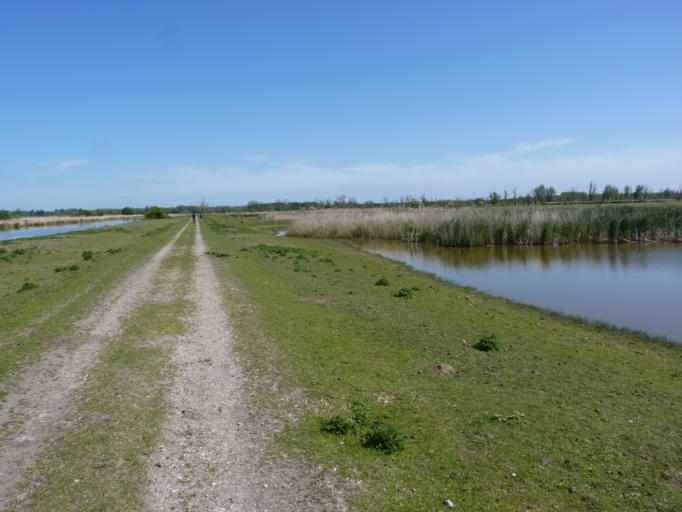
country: NL
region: Flevoland
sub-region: Gemeente Lelystad
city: Lelystad
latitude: 52.4567
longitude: 5.3963
